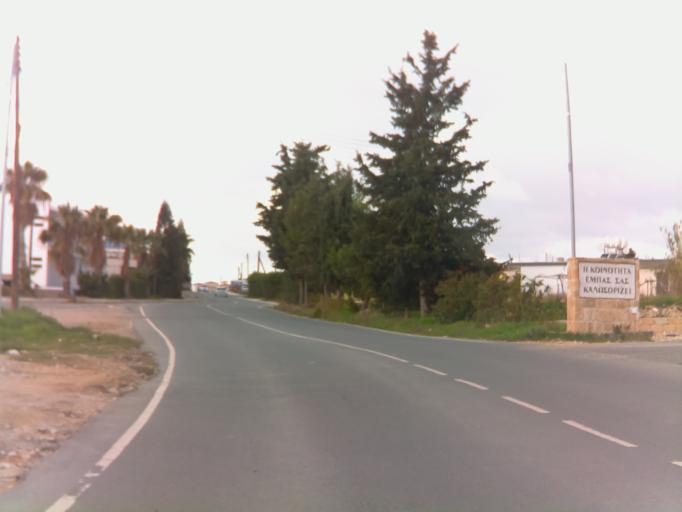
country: CY
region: Pafos
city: Empa
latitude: 34.7963
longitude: 32.4348
